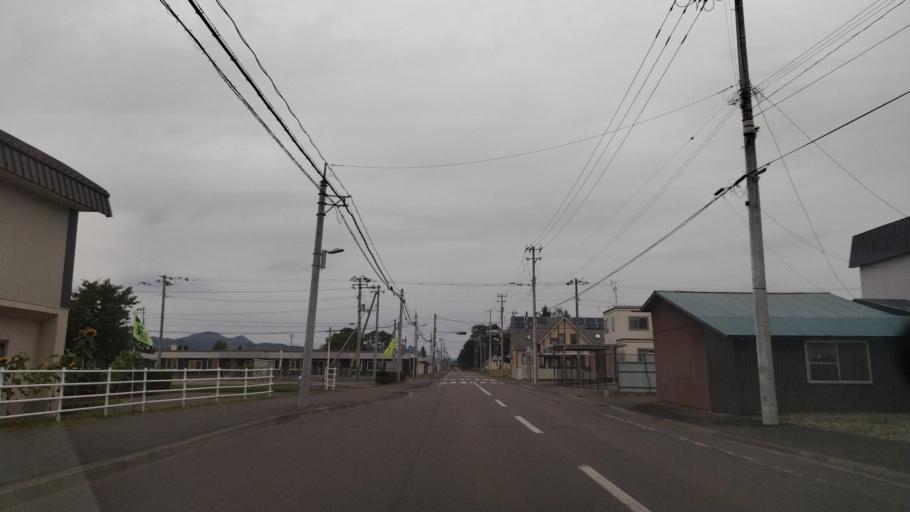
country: JP
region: Hokkaido
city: Otofuke
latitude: 43.2308
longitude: 143.2807
